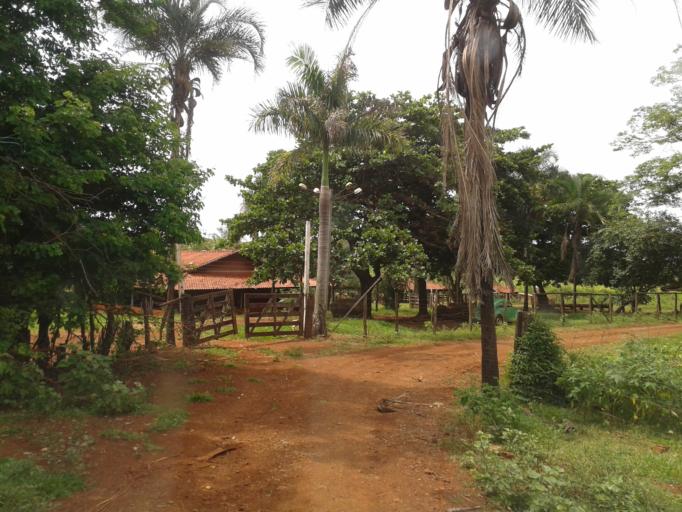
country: BR
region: Minas Gerais
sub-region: Centralina
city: Centralina
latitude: -18.6684
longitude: -49.2373
